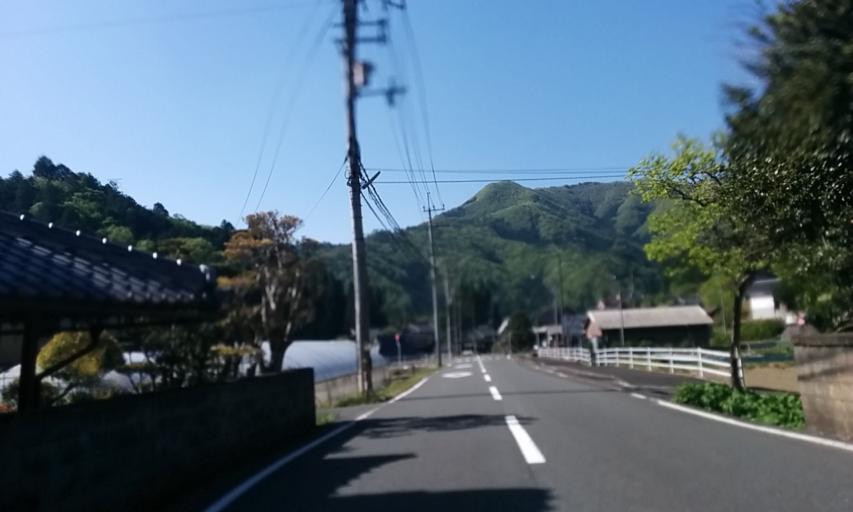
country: JP
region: Kyoto
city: Ayabe
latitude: 35.2603
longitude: 135.4533
